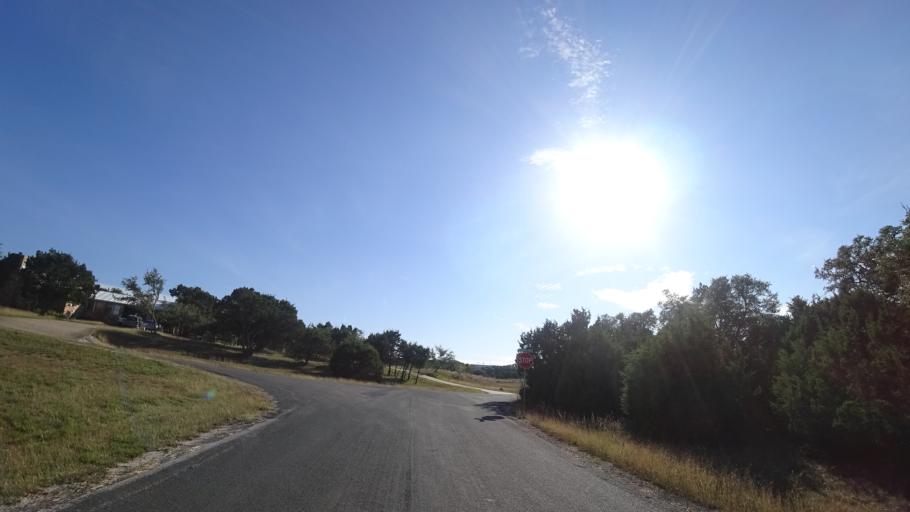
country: US
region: Texas
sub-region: Travis County
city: Bee Cave
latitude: 30.2352
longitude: -97.9303
